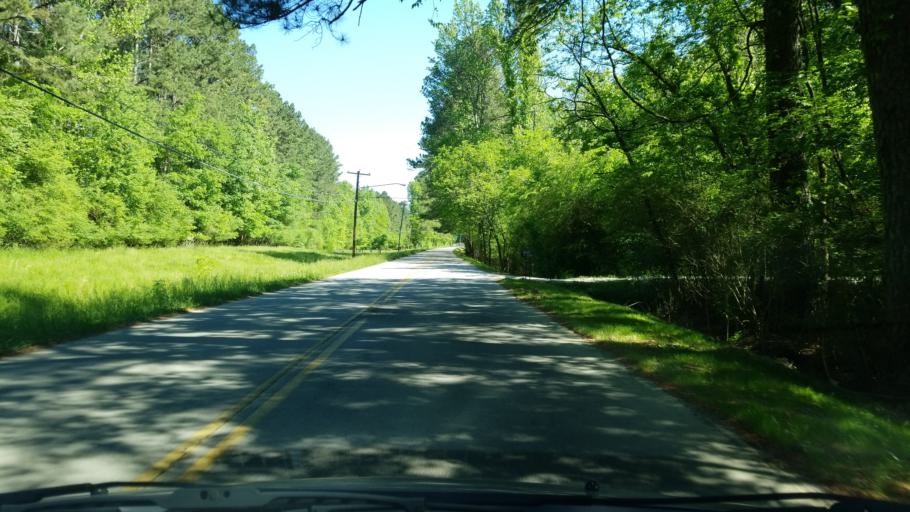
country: US
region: Tennessee
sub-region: Hamilton County
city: Chattanooga
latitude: 35.0380
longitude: -85.3345
